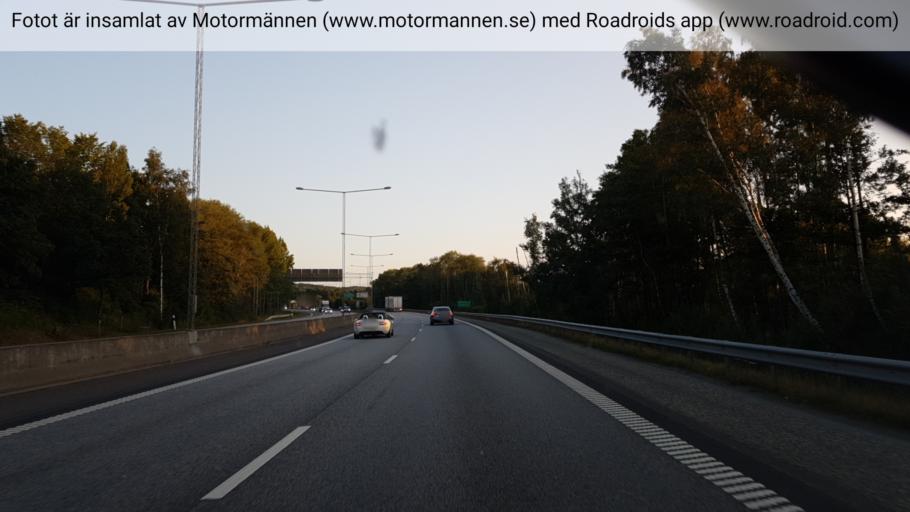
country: SE
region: Joenkoeping
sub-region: Jonkopings Kommun
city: Jonkoping
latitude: 57.7698
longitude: 14.1898
